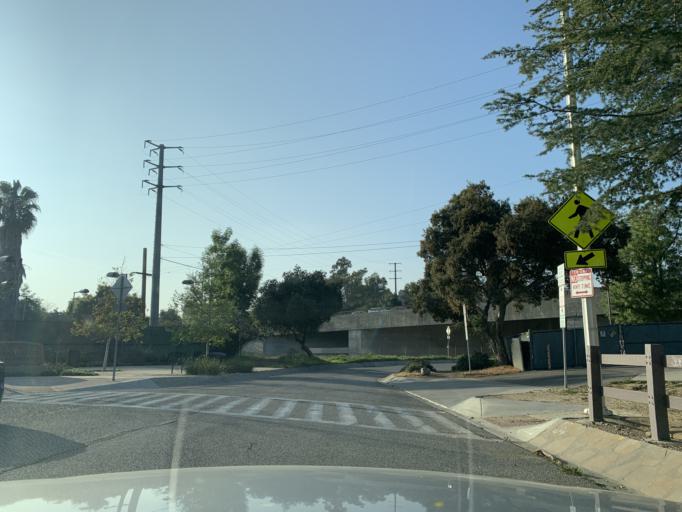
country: US
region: California
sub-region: Los Angeles County
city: South Pasadena
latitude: 34.1172
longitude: -118.1677
